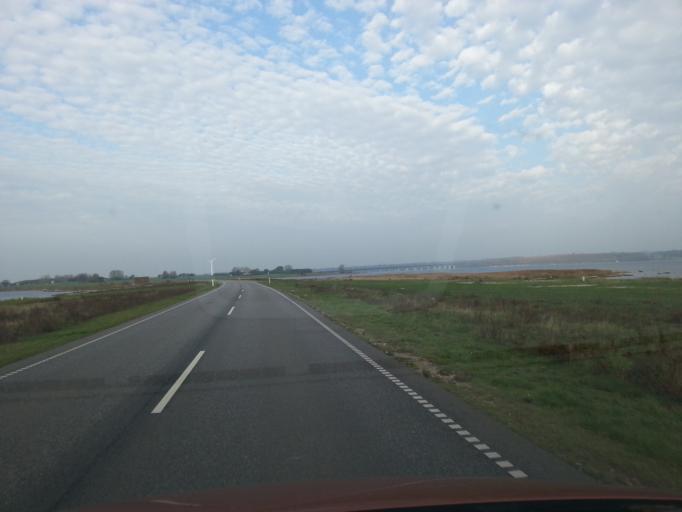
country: DK
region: Zealand
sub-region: Guldborgsund Kommune
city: Stubbekobing
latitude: 54.9405
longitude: 12.0001
